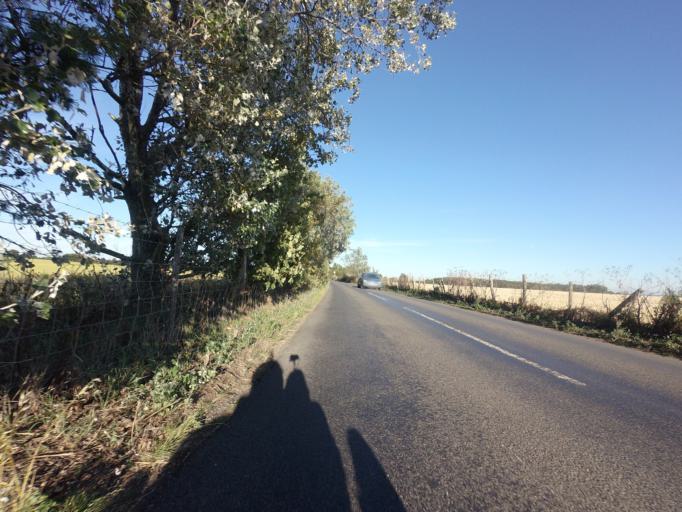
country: GB
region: England
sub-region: Kent
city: Herne Bay
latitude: 51.3518
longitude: 1.1710
